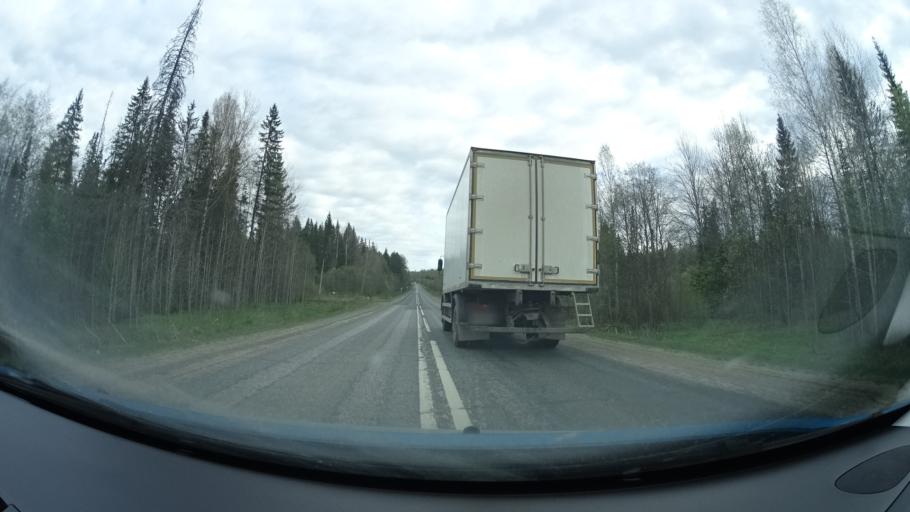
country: RU
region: Perm
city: Yugo-Kamskiy
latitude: 57.5254
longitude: 55.6842
